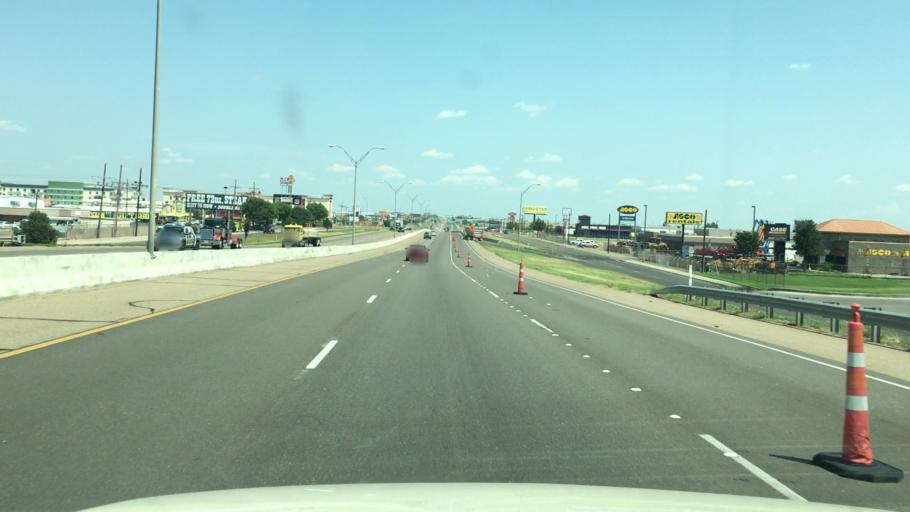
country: US
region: Texas
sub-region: Potter County
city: Amarillo
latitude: 35.1926
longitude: -101.7585
